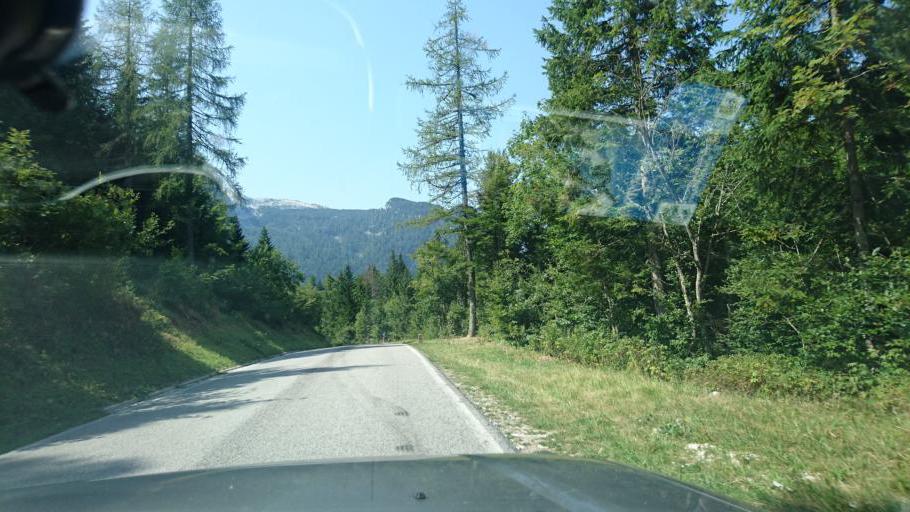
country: SI
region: Bovec
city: Bovec
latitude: 46.3907
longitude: 13.4838
